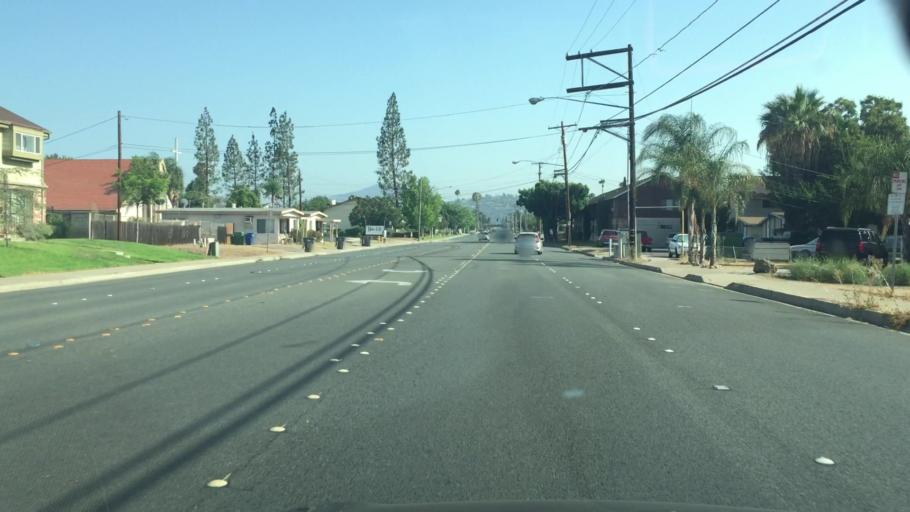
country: US
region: California
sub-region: San Diego County
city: Bostonia
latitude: 32.8114
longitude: -116.9510
